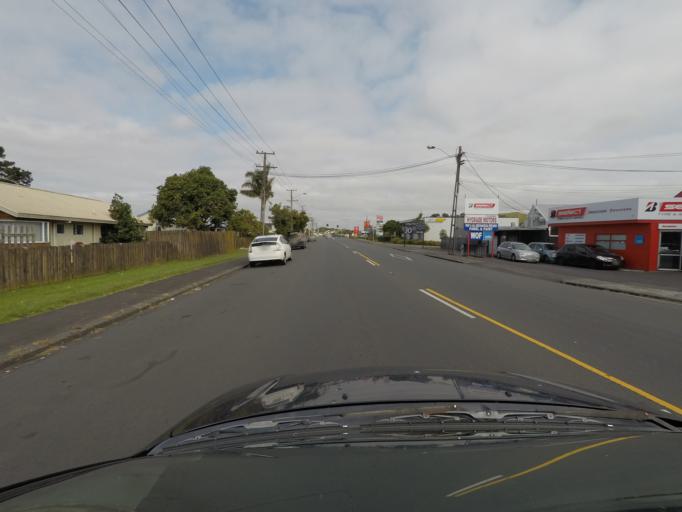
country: NZ
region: Auckland
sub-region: Auckland
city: Auckland
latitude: -36.9066
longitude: 174.7327
